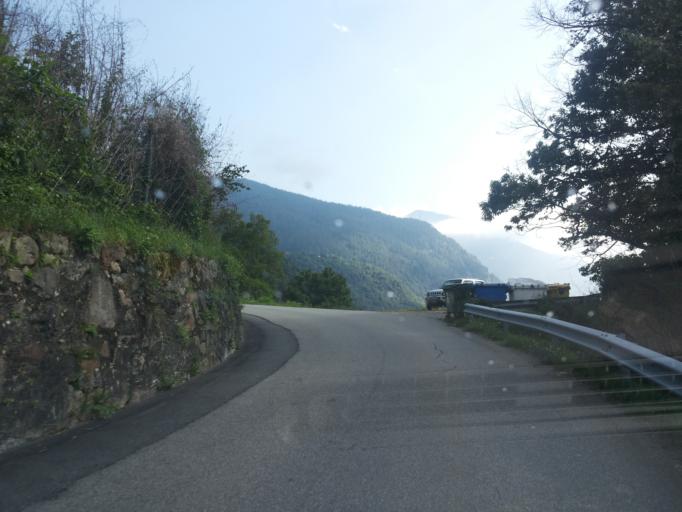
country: IT
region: Aosta Valley
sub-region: Valle d'Aosta
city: Fontainemore
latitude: 45.6514
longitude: 7.8645
